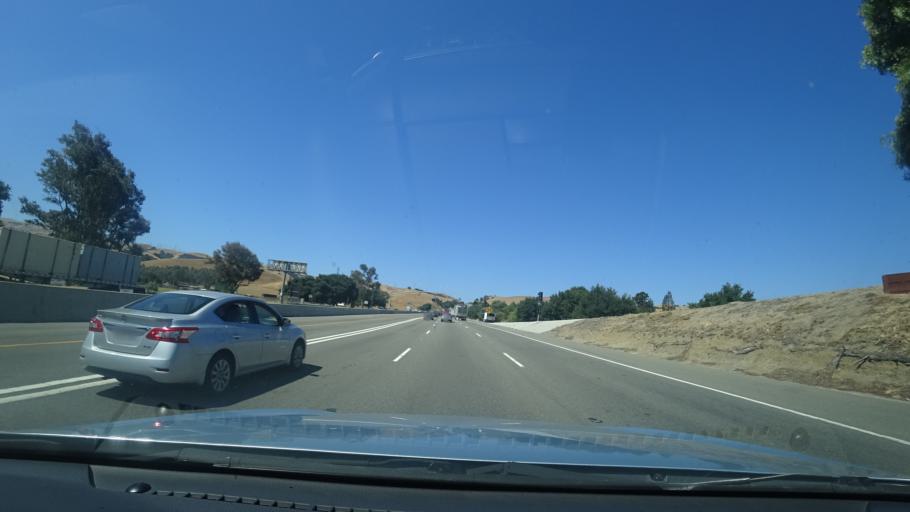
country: US
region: California
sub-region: Alameda County
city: Pleasanton
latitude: 37.5742
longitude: -121.8861
